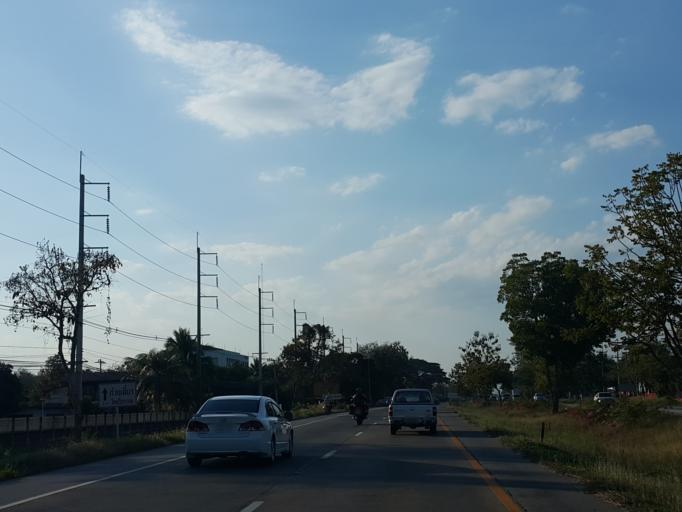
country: TH
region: Lampang
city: Lampang
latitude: 18.2943
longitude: 99.4193
